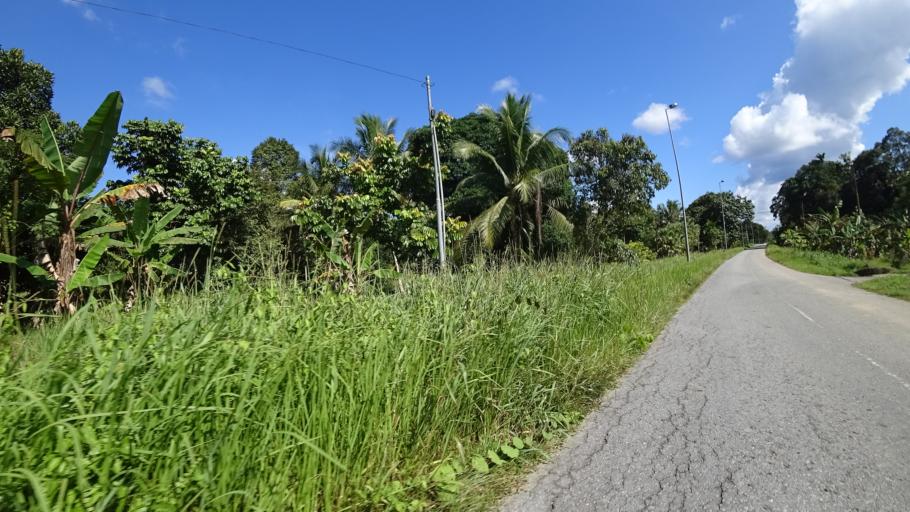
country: BN
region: Tutong
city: Tutong
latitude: 4.7444
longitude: 114.7875
